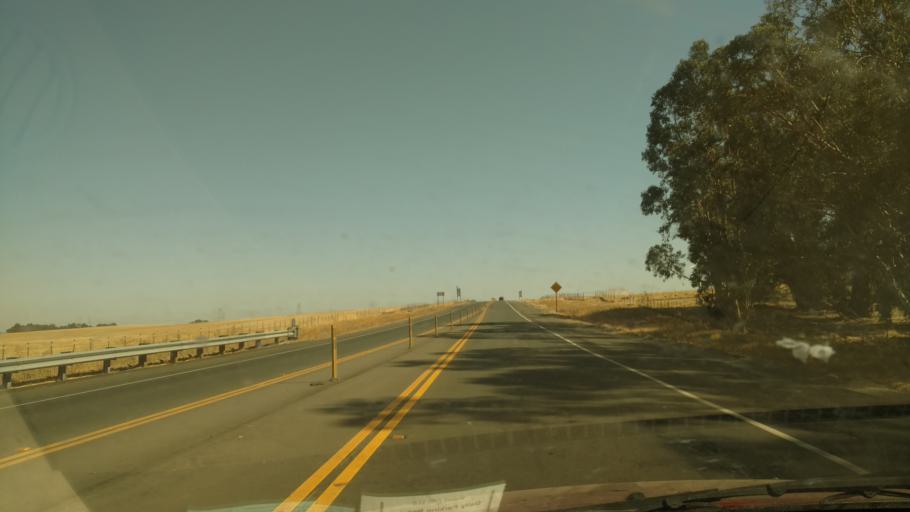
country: US
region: California
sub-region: Solano County
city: Rio Vista
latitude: 38.1835
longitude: -121.7685
